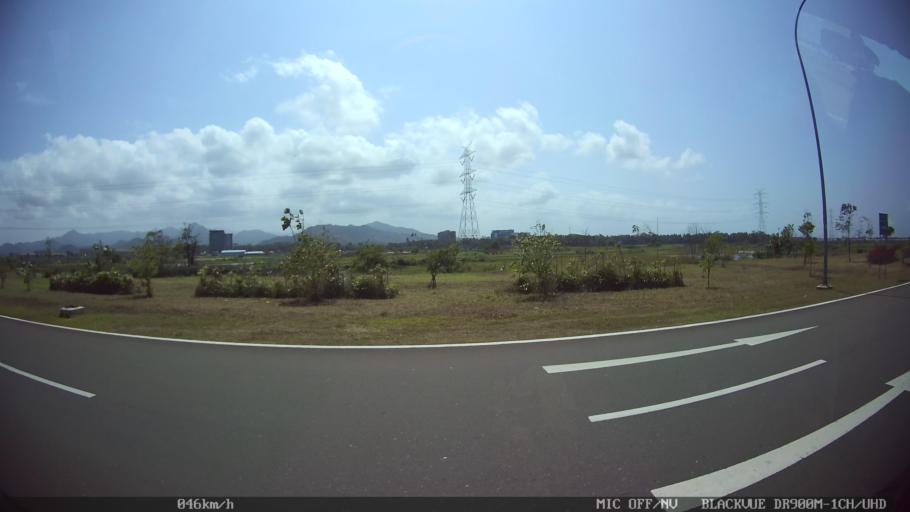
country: ID
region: Daerah Istimewa Yogyakarta
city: Srandakan
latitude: -7.8925
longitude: 110.0628
